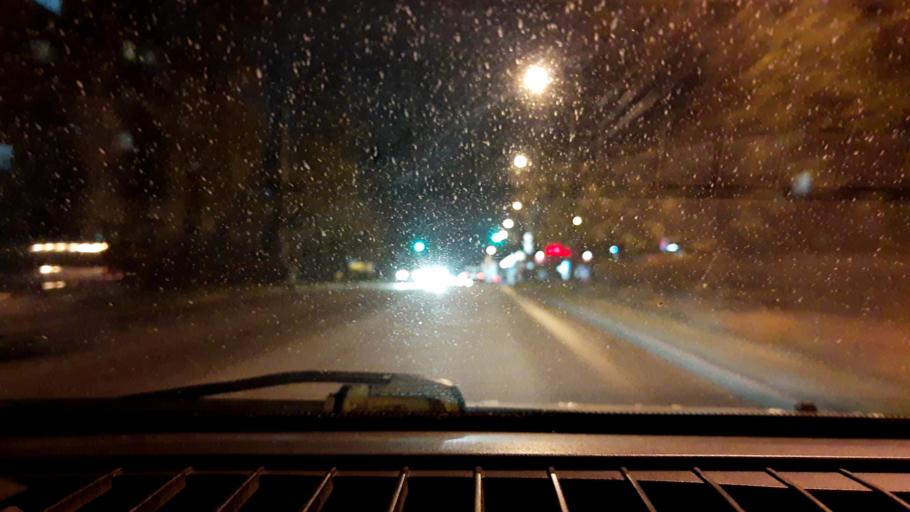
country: RU
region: Nizjnij Novgorod
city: Neklyudovo
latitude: 56.3607
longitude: 43.8467
